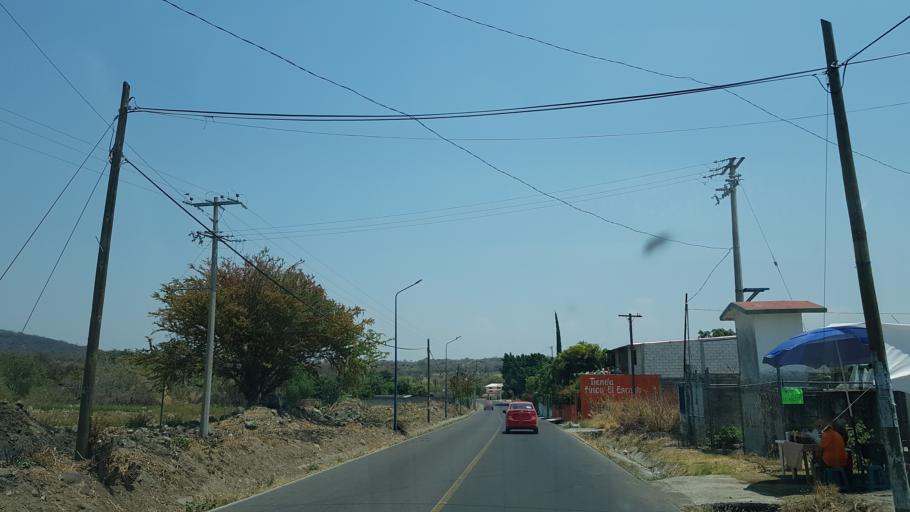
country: MX
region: Puebla
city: Huaquechula
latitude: 18.7635
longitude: -98.5263
